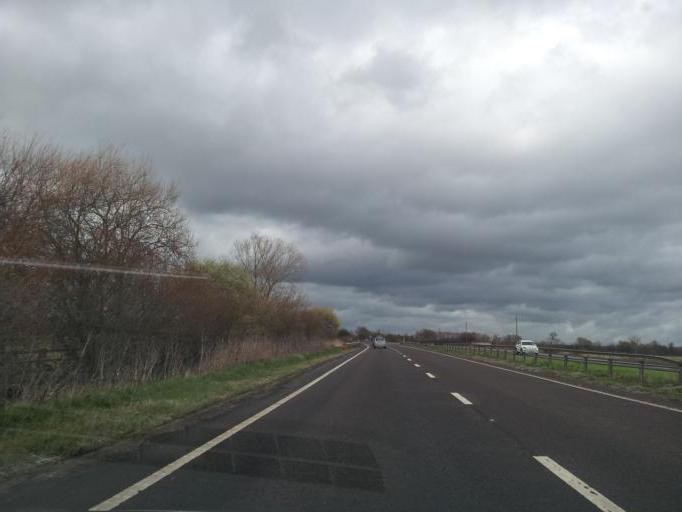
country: GB
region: England
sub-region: Somerset
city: Ilchester
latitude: 50.9910
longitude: -2.7009
